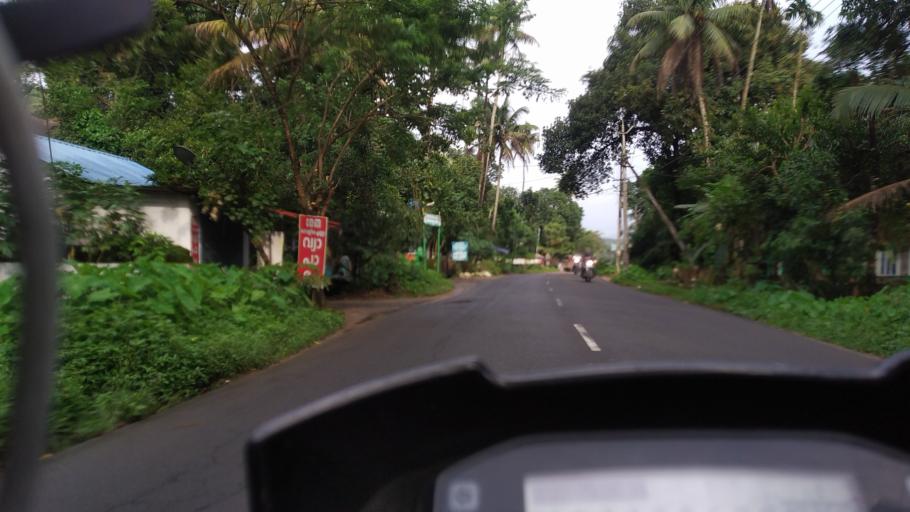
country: IN
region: Kerala
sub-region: Ernakulam
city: Kotamangalam
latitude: 10.0555
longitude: 76.6977
